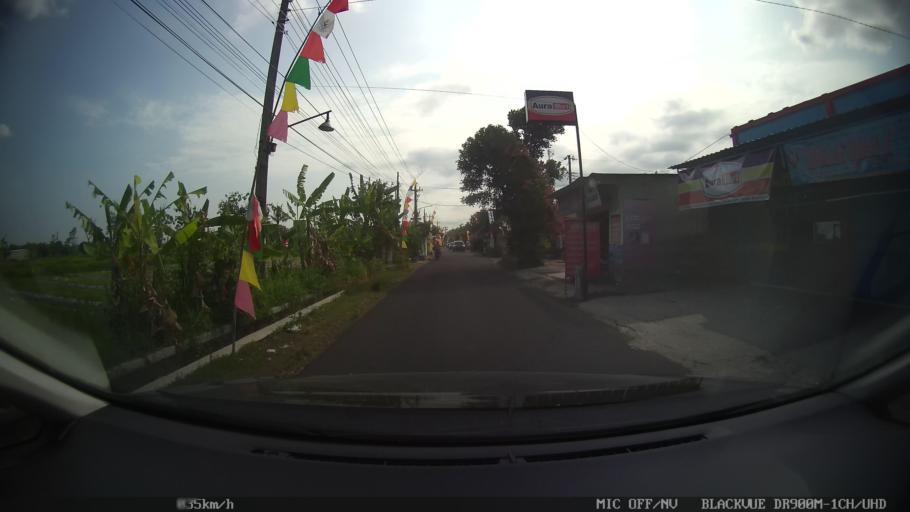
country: ID
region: Daerah Istimewa Yogyakarta
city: Depok
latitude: -7.7370
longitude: 110.4478
